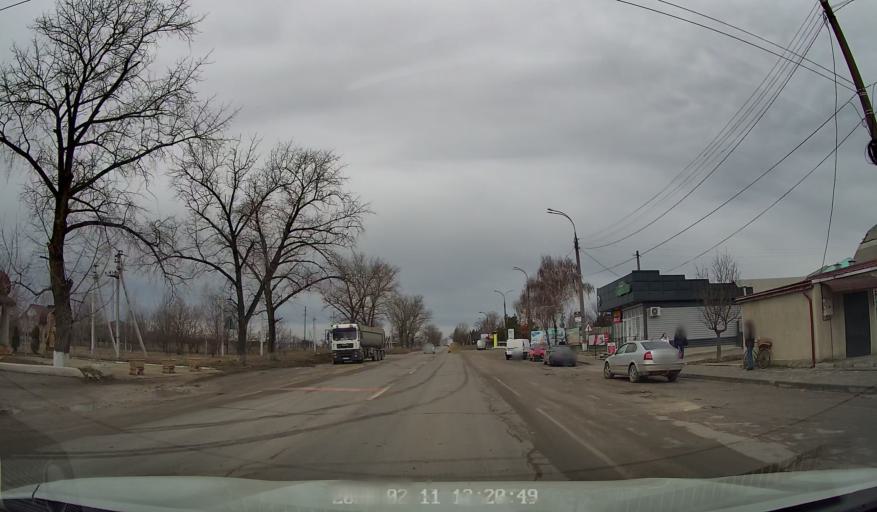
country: MD
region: Raionul Edinet
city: Edinet
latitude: 48.1185
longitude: 27.3827
